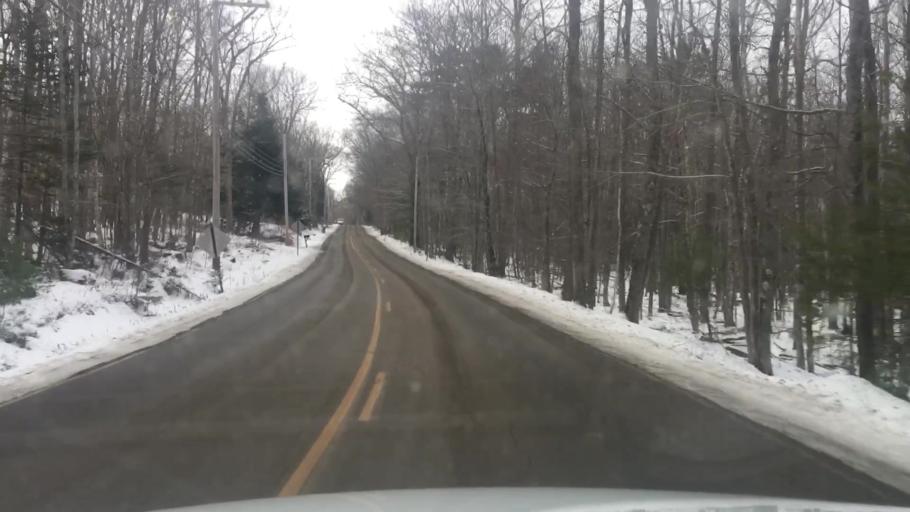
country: US
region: Maine
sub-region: Waldo County
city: Lincolnville
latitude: 44.2916
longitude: -69.0734
